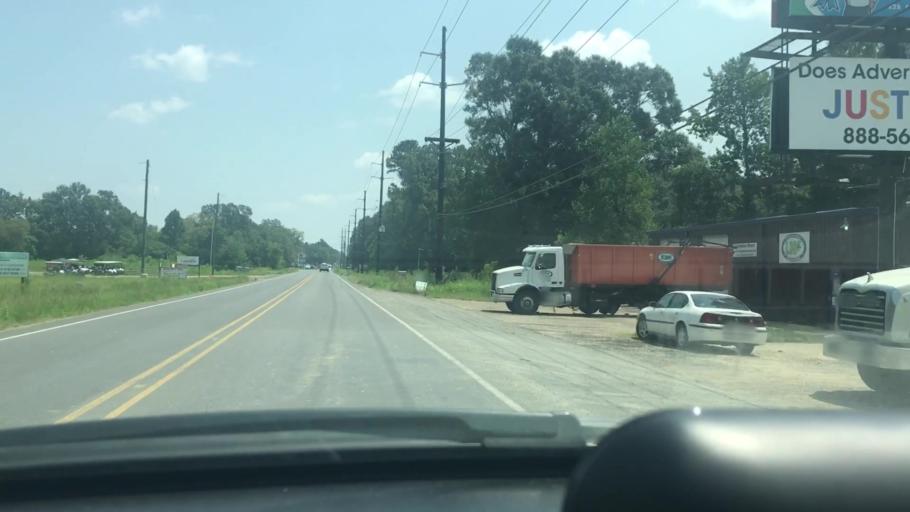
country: US
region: Louisiana
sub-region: Livingston Parish
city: Denham Springs
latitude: 30.4830
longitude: -90.9110
